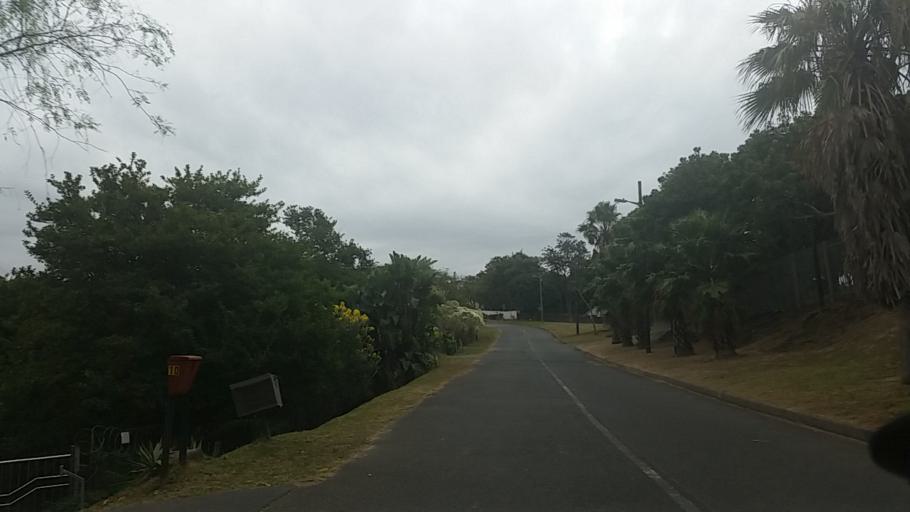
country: ZA
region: KwaZulu-Natal
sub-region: eThekwini Metropolitan Municipality
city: Berea
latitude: -29.8466
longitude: 30.9326
